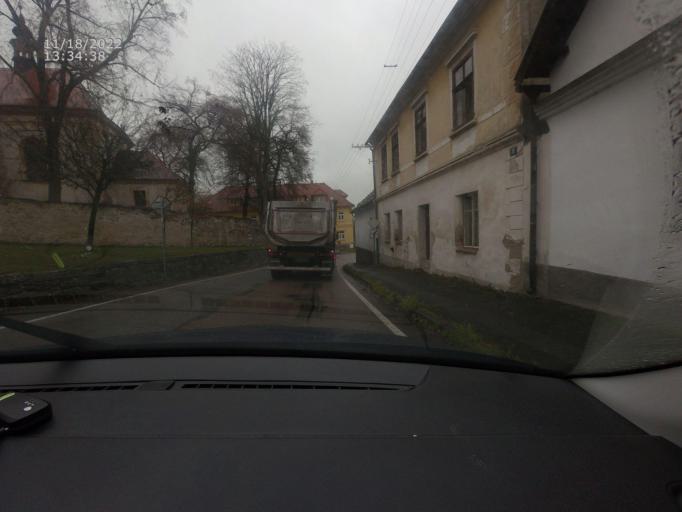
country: CZ
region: Plzensky
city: Kasejovice
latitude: 49.4029
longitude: 13.7751
